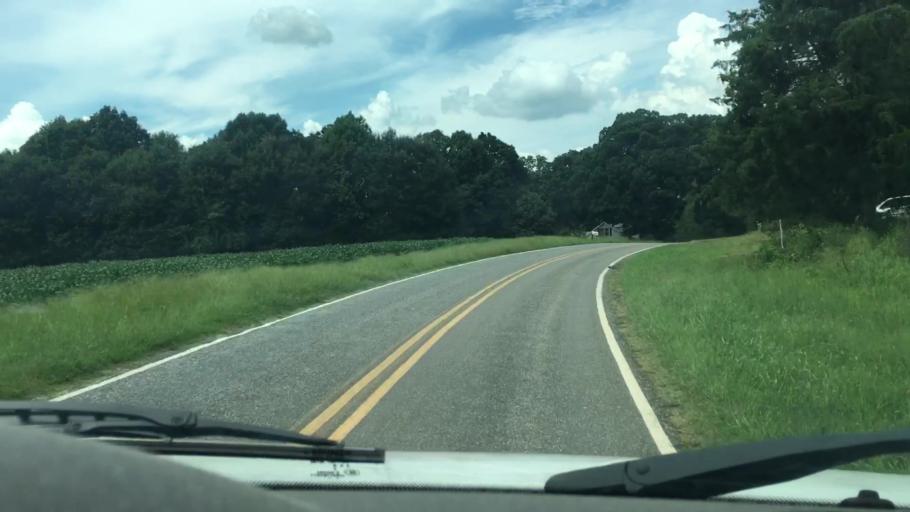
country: US
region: North Carolina
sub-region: Iredell County
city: Troutman
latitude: 35.6672
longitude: -80.8313
